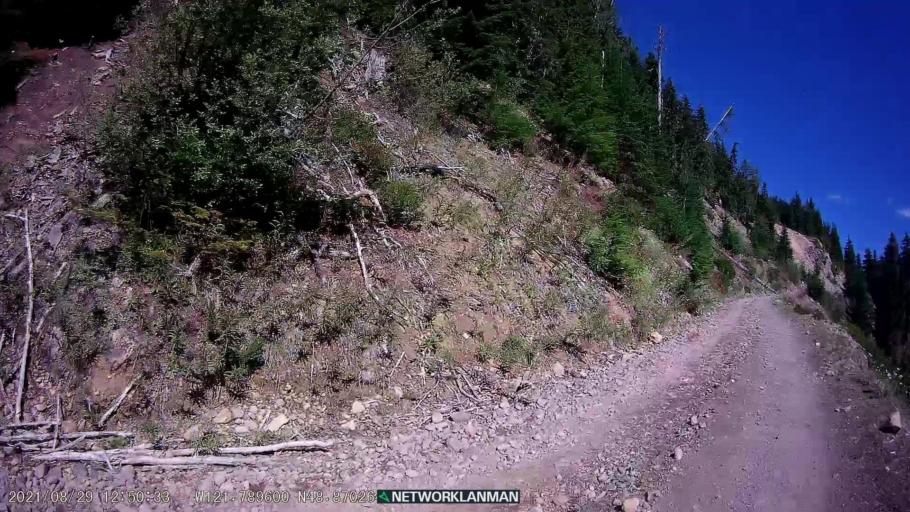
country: CA
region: British Columbia
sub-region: Fraser Valley Regional District
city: Chilliwack
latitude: 48.8705
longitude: -121.7896
